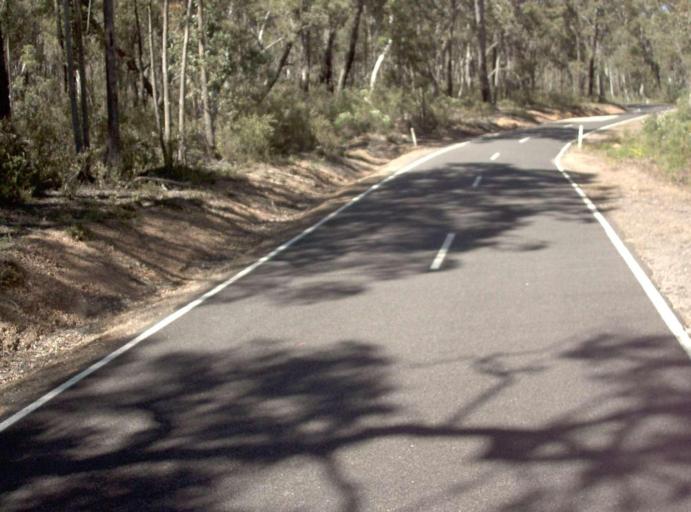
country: AU
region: New South Wales
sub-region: Bombala
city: Bombala
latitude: -37.1374
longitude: 148.7357
